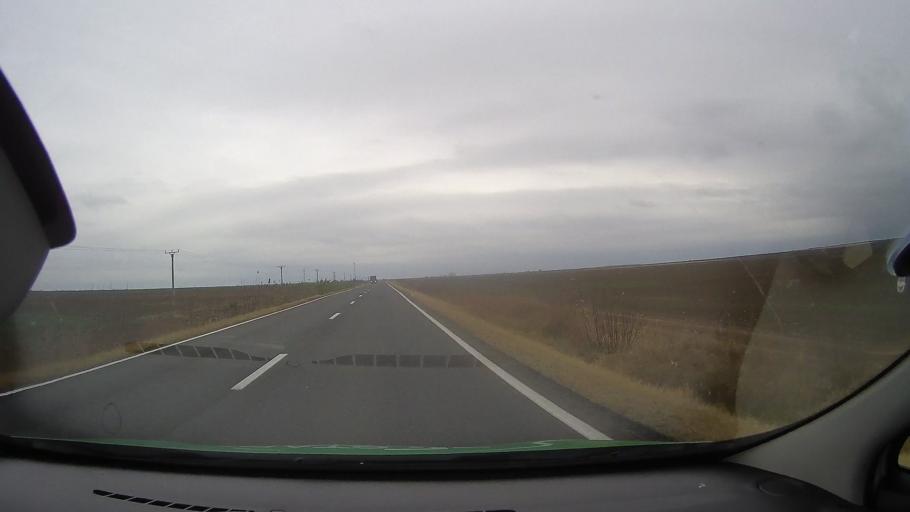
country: RO
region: Constanta
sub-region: Comuna Nicolae Balcescu
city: Nicolae Balcescu
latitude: 44.3786
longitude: 28.4135
